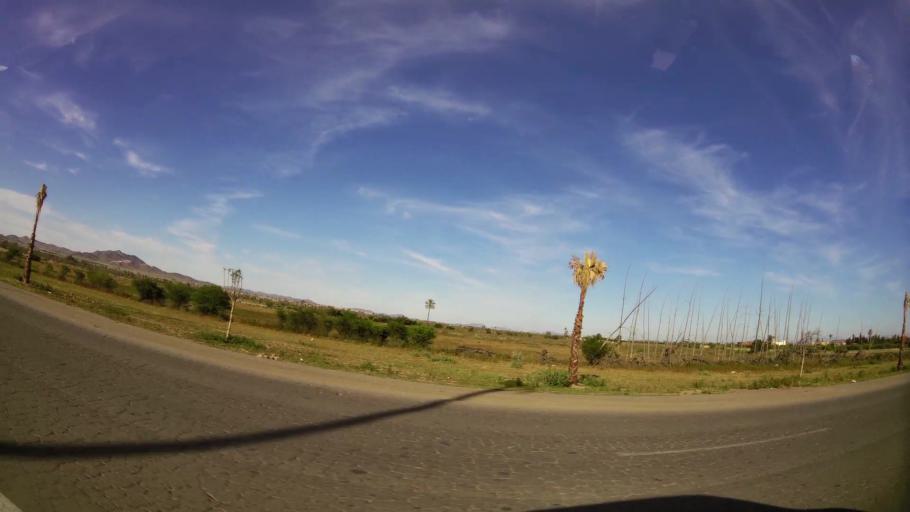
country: MA
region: Marrakech-Tensift-Al Haouz
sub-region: Marrakech
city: Marrakesh
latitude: 31.6855
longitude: -8.0519
